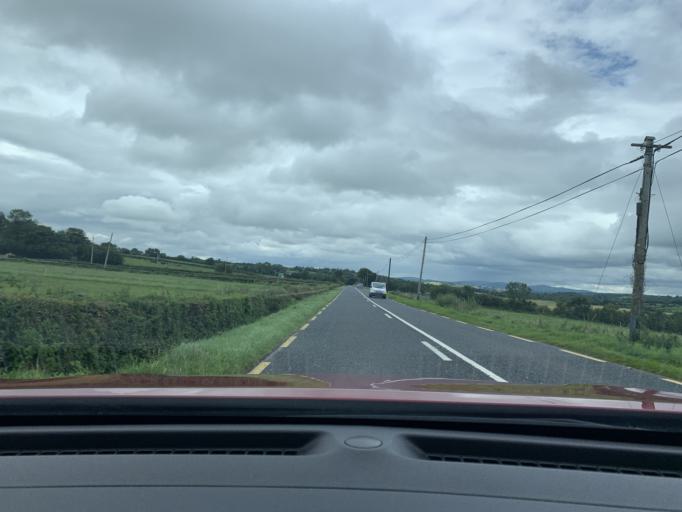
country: IE
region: Ulster
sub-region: County Donegal
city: Convoy
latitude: 54.7979
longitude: -7.6628
